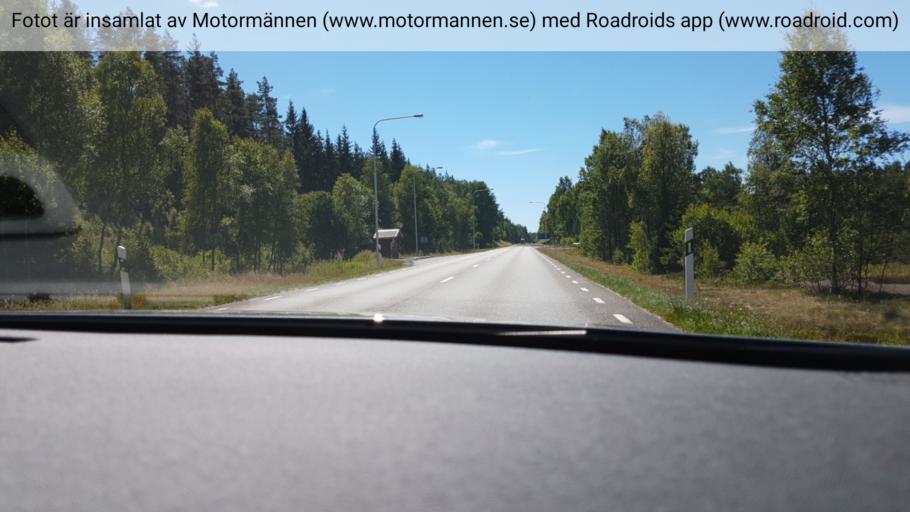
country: SE
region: Joenkoeping
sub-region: Gnosjo Kommun
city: Marieholm
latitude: 57.6024
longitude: 13.7483
